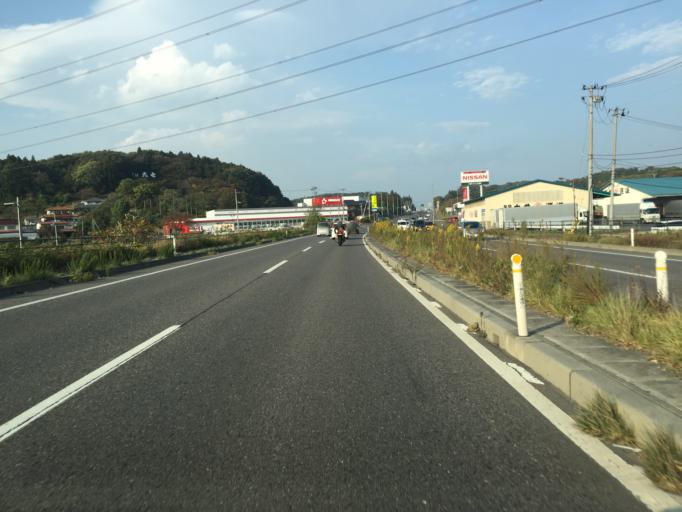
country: JP
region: Fukushima
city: Motomiya
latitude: 37.5435
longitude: 140.3975
